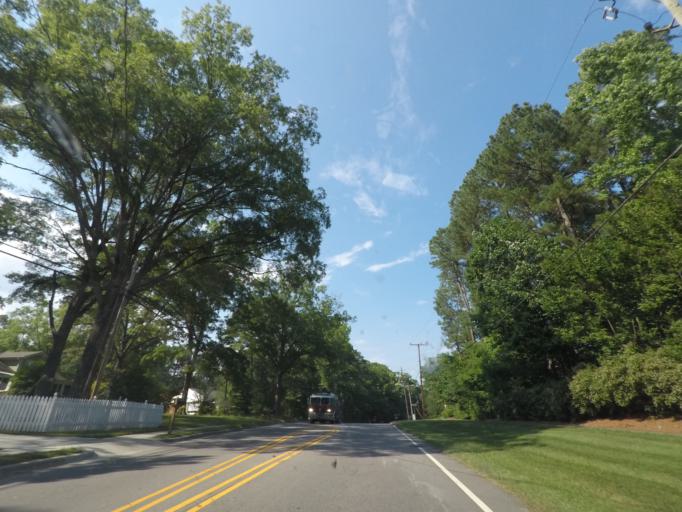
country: US
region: North Carolina
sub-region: Durham County
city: Durham
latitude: 35.9325
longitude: -78.9512
